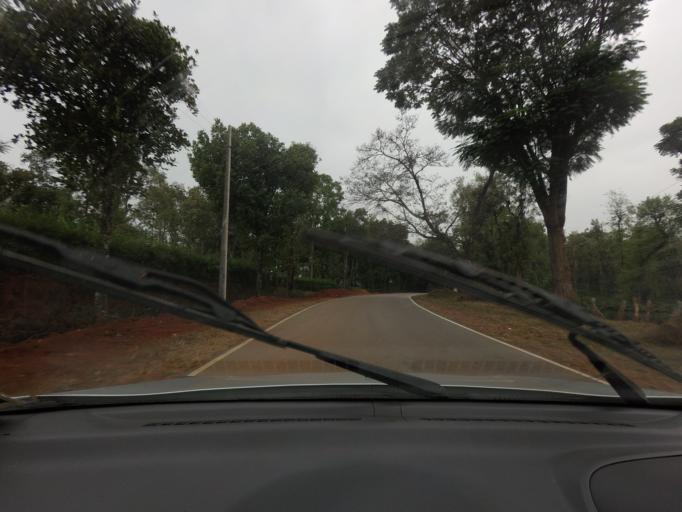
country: IN
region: Karnataka
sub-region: Hassan
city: Sakleshpur
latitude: 12.9459
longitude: 75.7512
